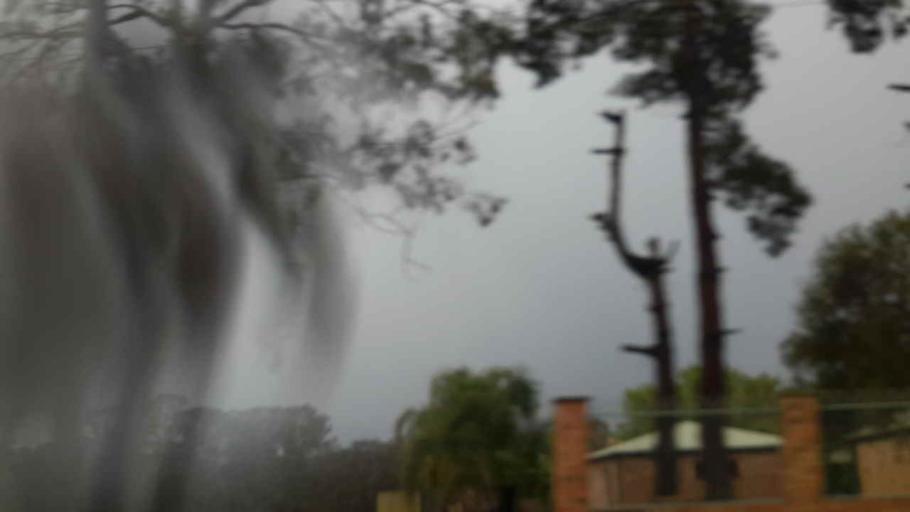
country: AU
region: New South Wales
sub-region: Wollondilly
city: Douglas Park
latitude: -34.2052
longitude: 150.7193
